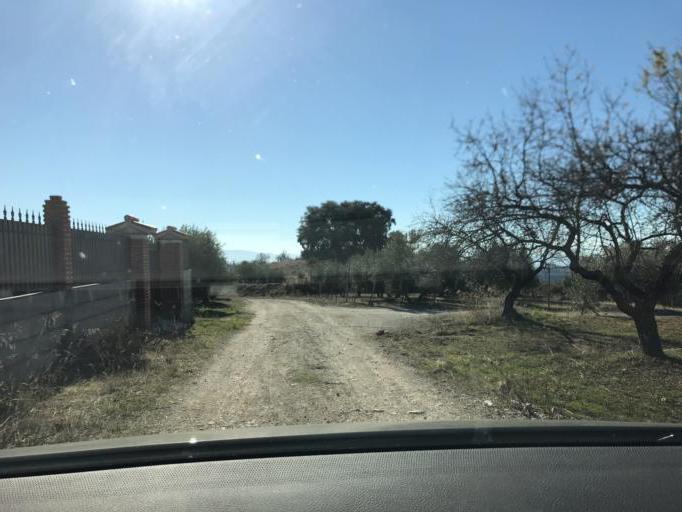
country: ES
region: Andalusia
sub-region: Provincia de Granada
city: Viznar
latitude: 37.2205
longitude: -3.5538
